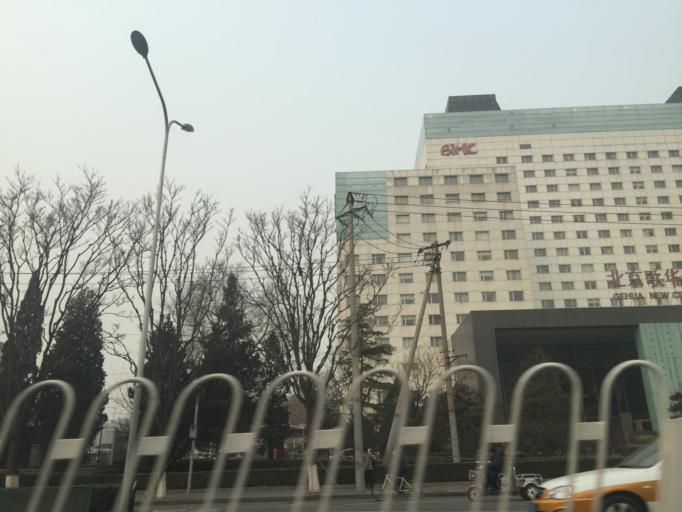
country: CN
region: Beijing
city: Datun
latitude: 39.9633
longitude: 116.3886
